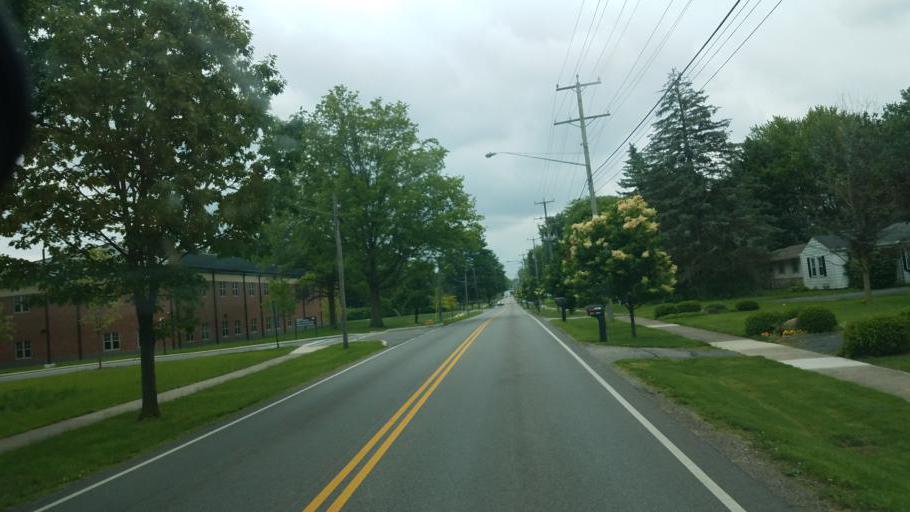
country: US
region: Ohio
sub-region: Delaware County
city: Delaware
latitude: 40.3099
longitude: -83.0896
